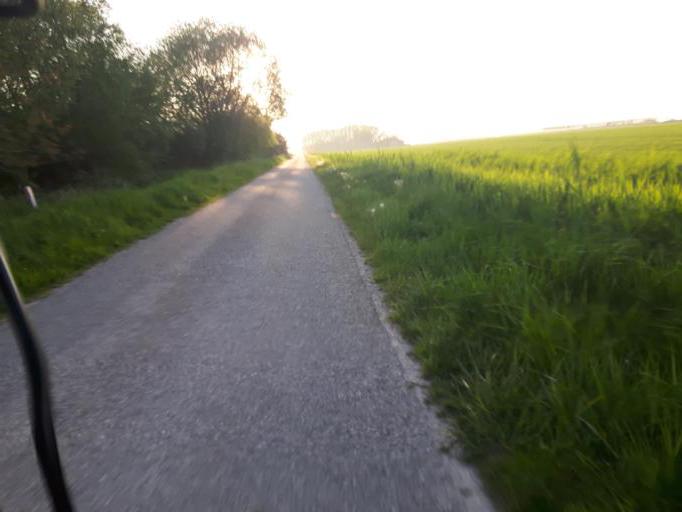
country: NL
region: Zeeland
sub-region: Gemeente Goes
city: Goes
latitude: 51.5056
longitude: 3.8296
